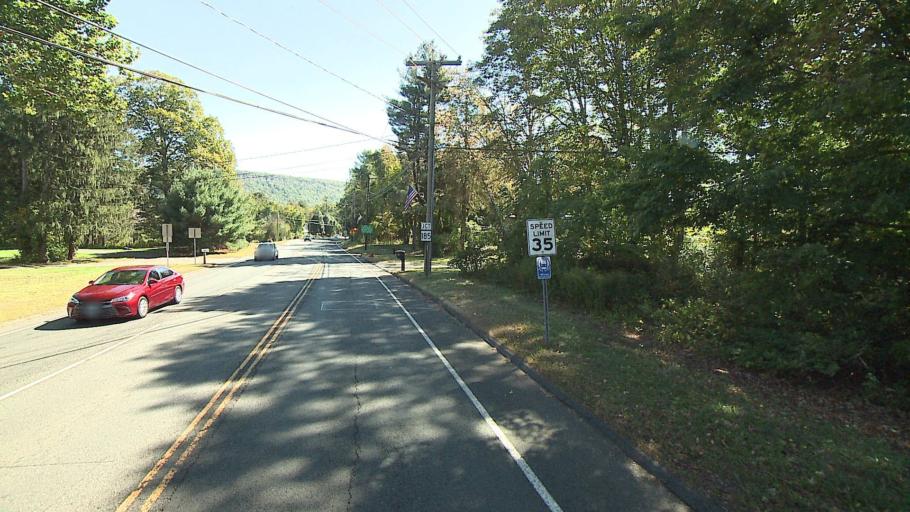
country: US
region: Connecticut
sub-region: Hartford County
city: Weatogue
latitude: 41.8487
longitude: -72.8126
